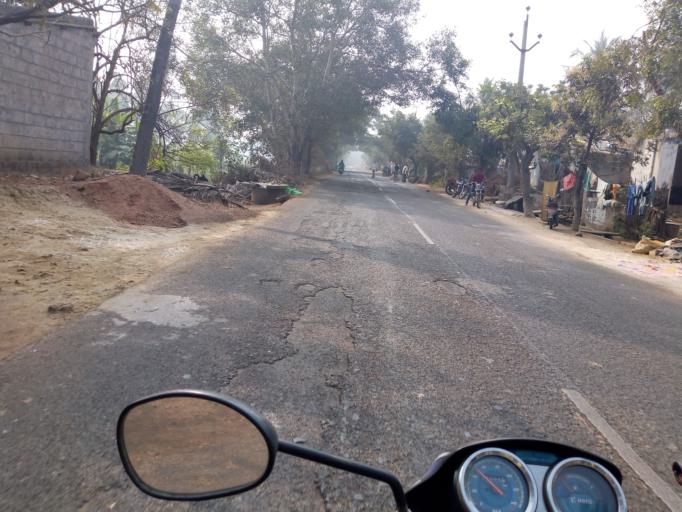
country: IN
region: Andhra Pradesh
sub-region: West Godavari
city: Tadepallegudem
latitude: 16.7842
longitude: 81.4197
